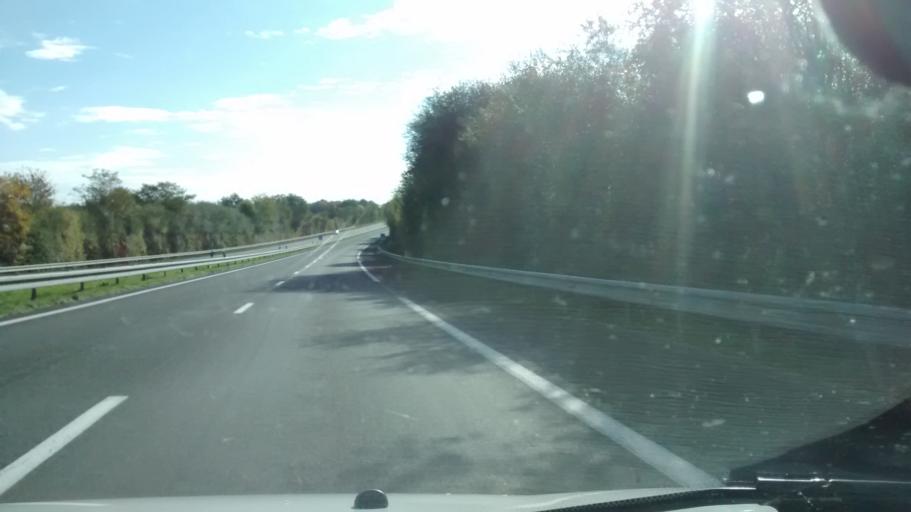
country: FR
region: Pays de la Loire
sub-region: Departement de Maine-et-Loire
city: Pouance
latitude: 47.7530
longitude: -1.1615
